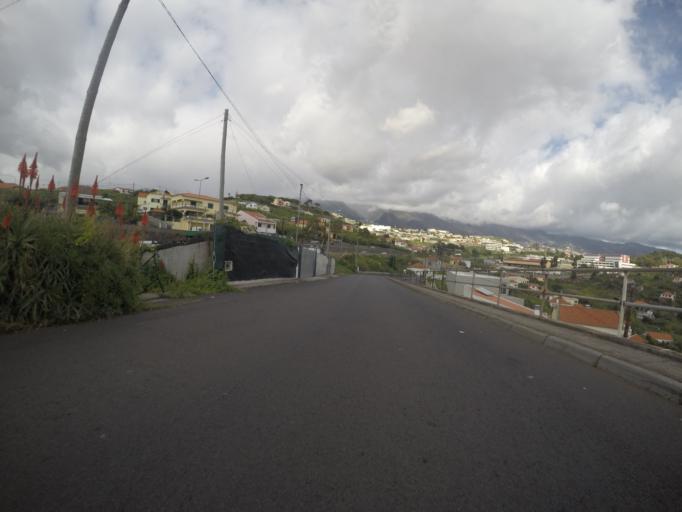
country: PT
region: Madeira
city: Camara de Lobos
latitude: 32.6486
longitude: -16.9494
